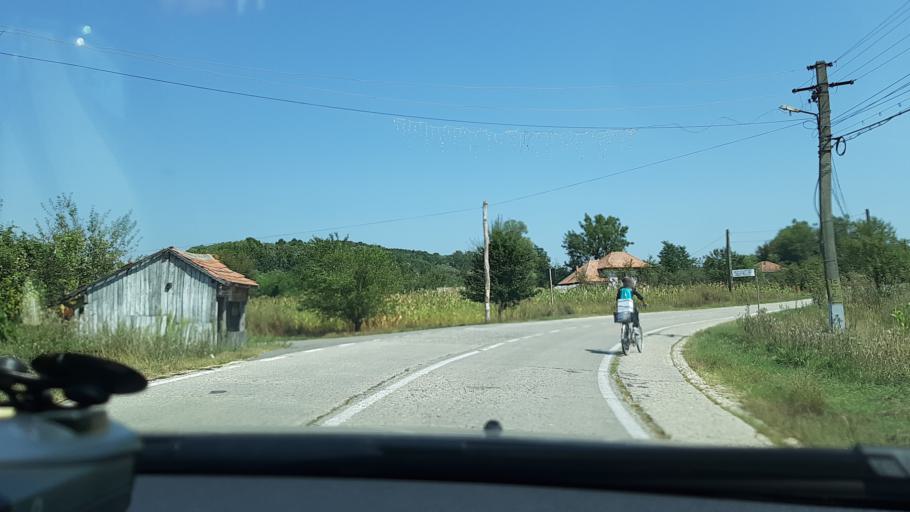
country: RO
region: Gorj
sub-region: Comuna Logresti-Mosteni
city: Logresti Mosteni
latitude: 44.8990
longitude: 23.7329
